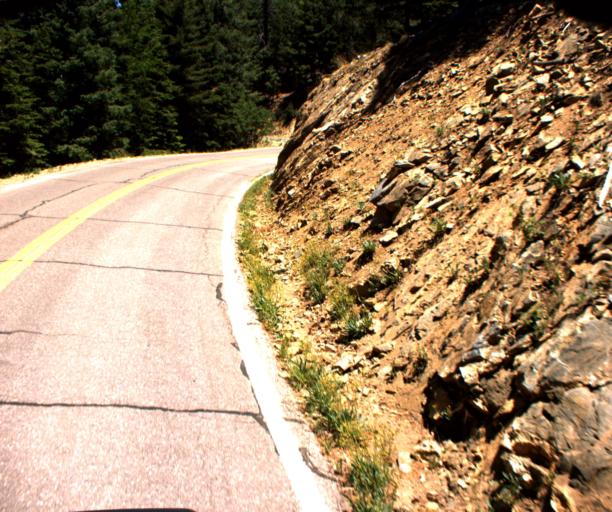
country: US
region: Arizona
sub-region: Graham County
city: Swift Trail Junction
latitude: 32.6530
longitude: -109.8604
